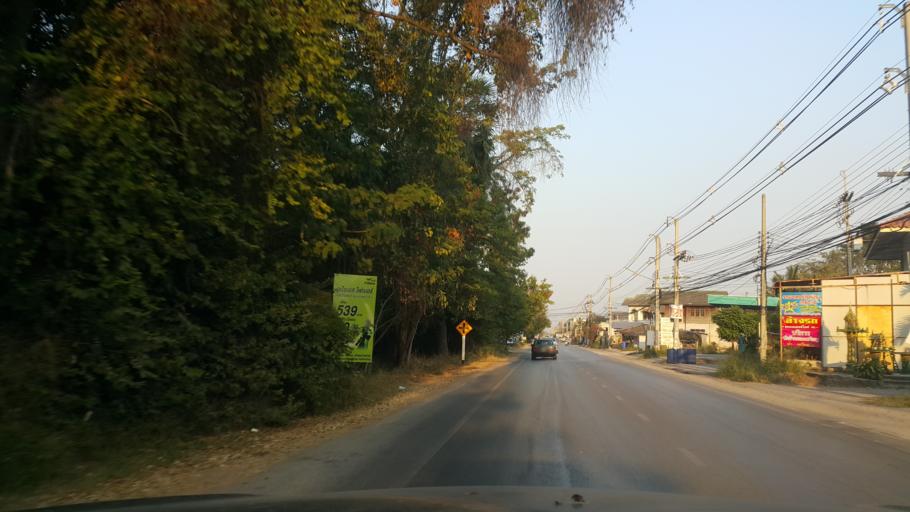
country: TH
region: Nakhon Ratchasima
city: Nakhon Ratchasima
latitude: 14.9384
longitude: 102.0318
